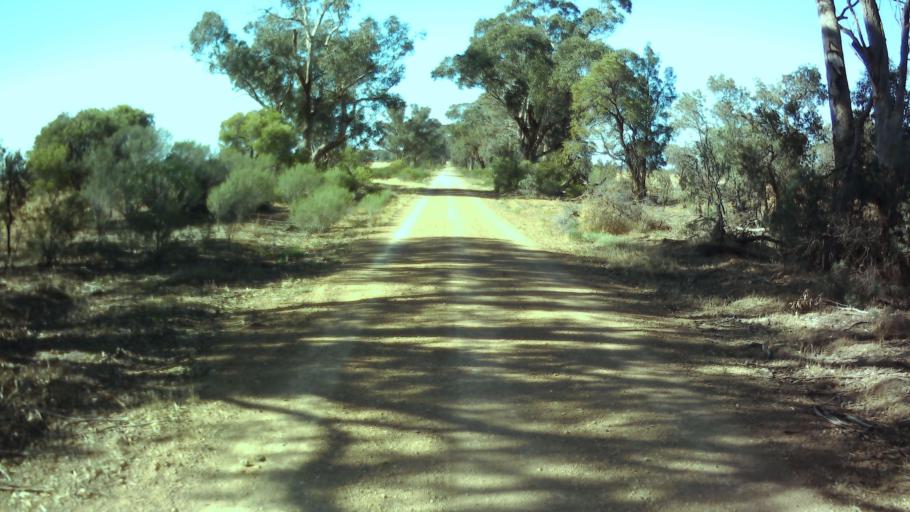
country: AU
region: New South Wales
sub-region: Weddin
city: Grenfell
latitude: -33.9163
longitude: 147.8757
